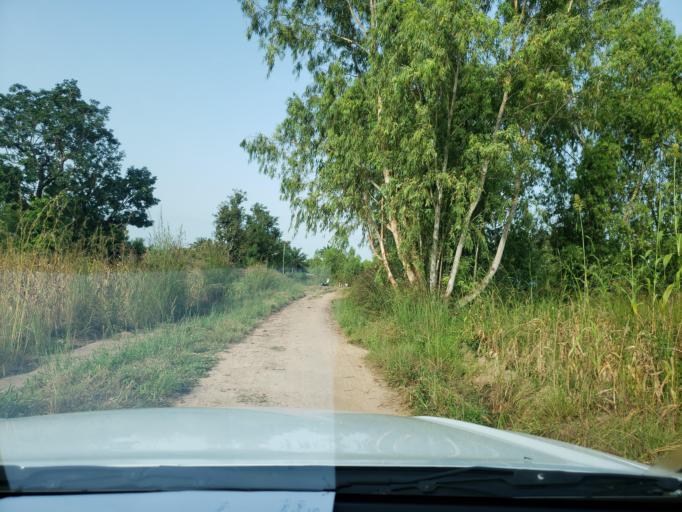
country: TG
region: Kara
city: Bafilo
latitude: 9.4105
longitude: 1.1811
